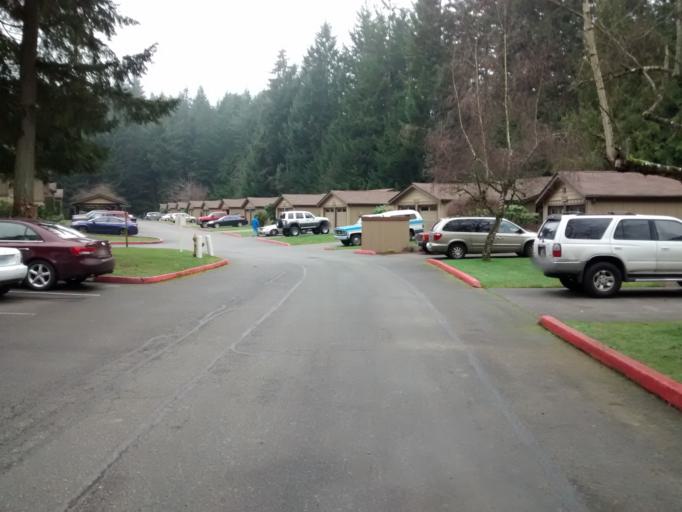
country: US
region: Washington
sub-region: Kitsap County
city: Parkwood
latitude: 47.5219
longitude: -122.6071
